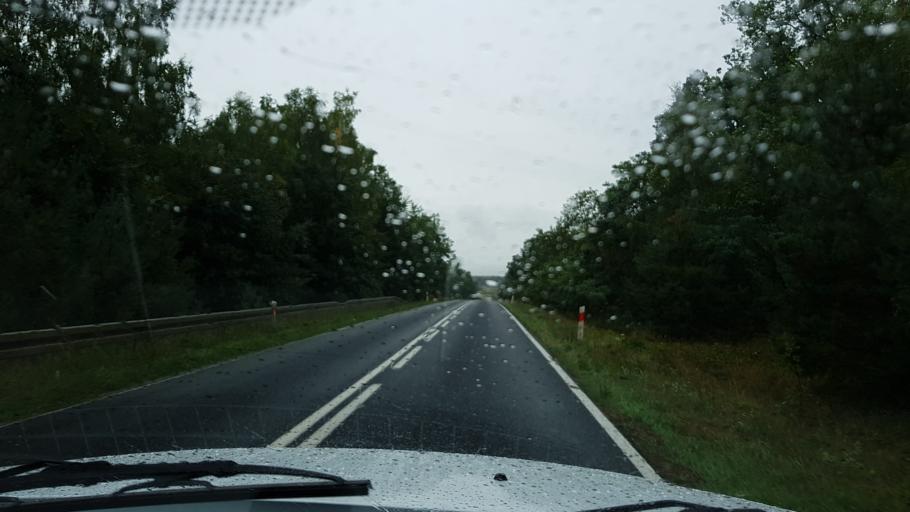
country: PL
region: West Pomeranian Voivodeship
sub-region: Powiat gryfinski
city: Widuchowa
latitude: 53.0688
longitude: 14.3660
